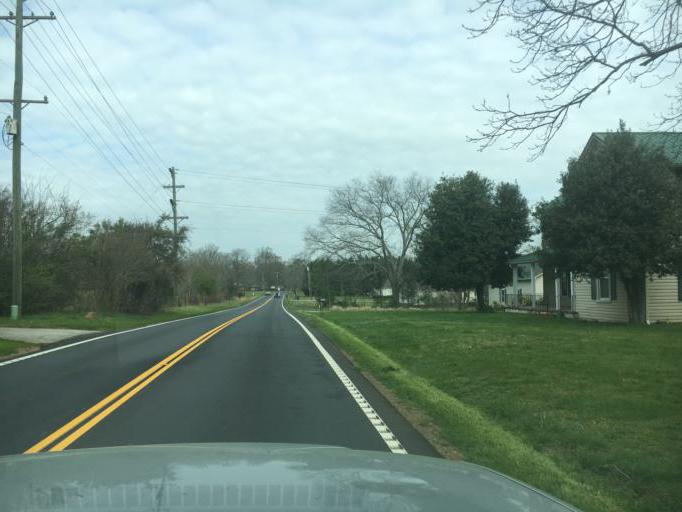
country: US
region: South Carolina
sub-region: Spartanburg County
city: Inman
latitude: 35.0060
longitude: -82.0721
